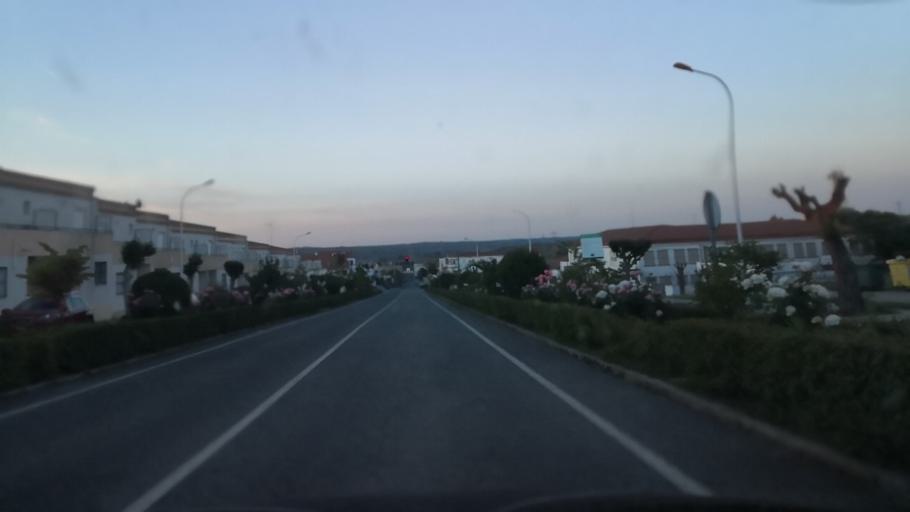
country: ES
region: Extremadura
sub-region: Provincia de Caceres
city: Alcantara
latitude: 39.7117
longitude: -6.8855
